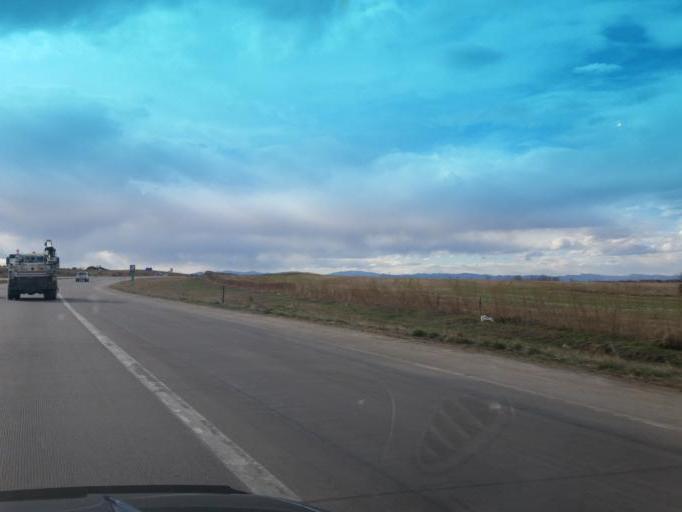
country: US
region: Colorado
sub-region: Weld County
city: Milliken
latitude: 40.3922
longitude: -104.7951
